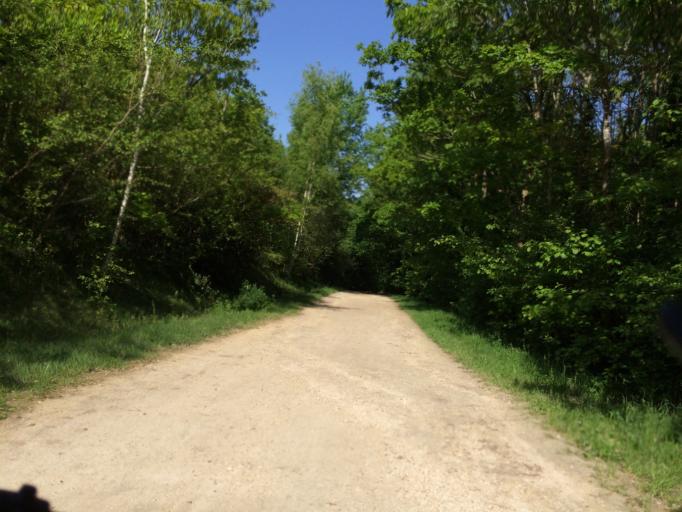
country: FR
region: Ile-de-France
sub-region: Departement des Hauts-de-Seine
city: Chatenay-Malabry
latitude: 48.7571
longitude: 2.2628
